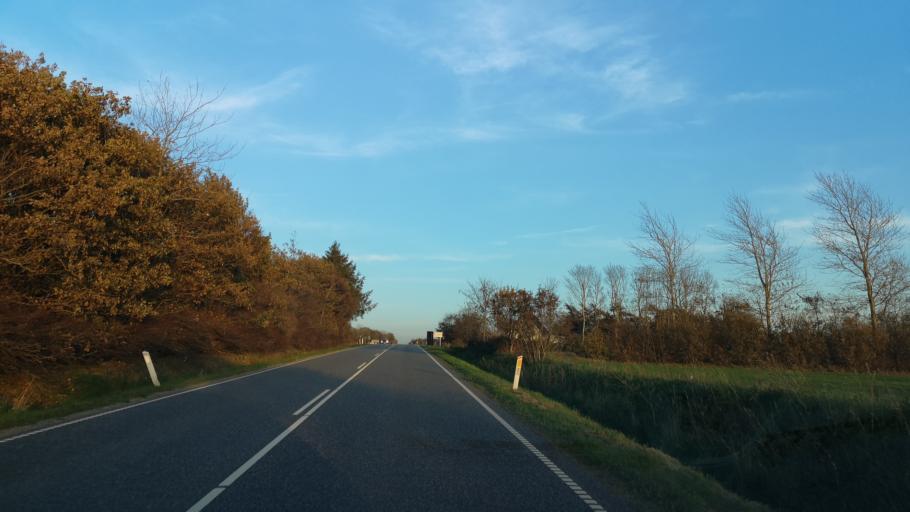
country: DK
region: Central Jutland
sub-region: Ringkobing-Skjern Kommune
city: Ringkobing
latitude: 56.0826
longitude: 8.3911
